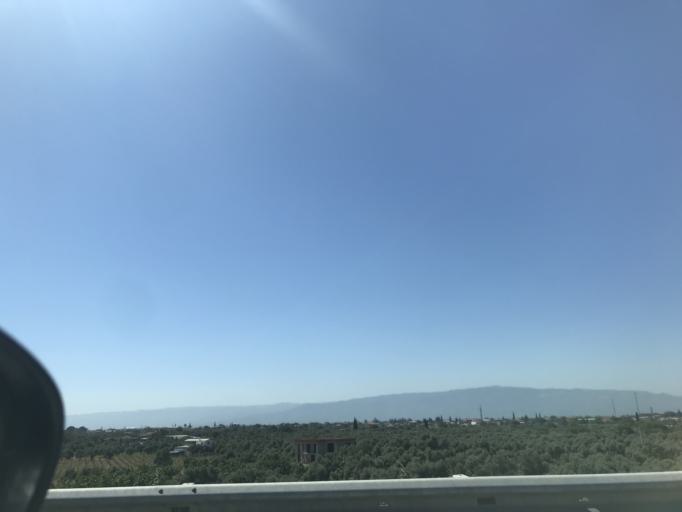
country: TR
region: Aydin
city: Incirliova
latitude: 37.8755
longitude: 27.6801
